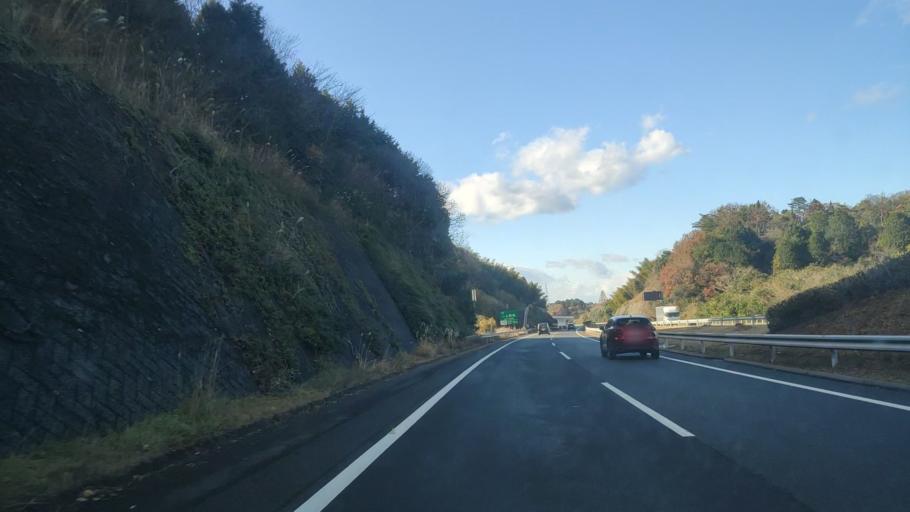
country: JP
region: Ehime
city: Saijo
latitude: 33.9091
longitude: 133.2510
